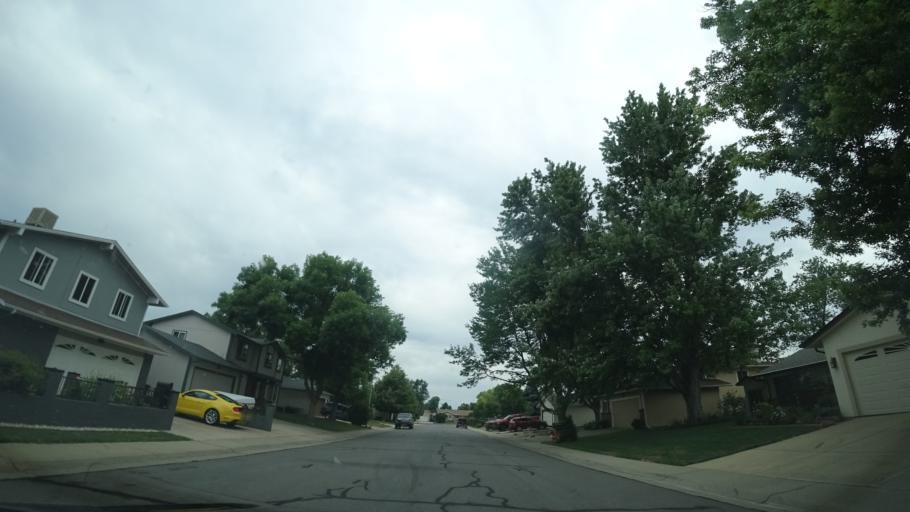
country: US
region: Colorado
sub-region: Jefferson County
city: Lakewood
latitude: 39.7056
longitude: -105.0985
